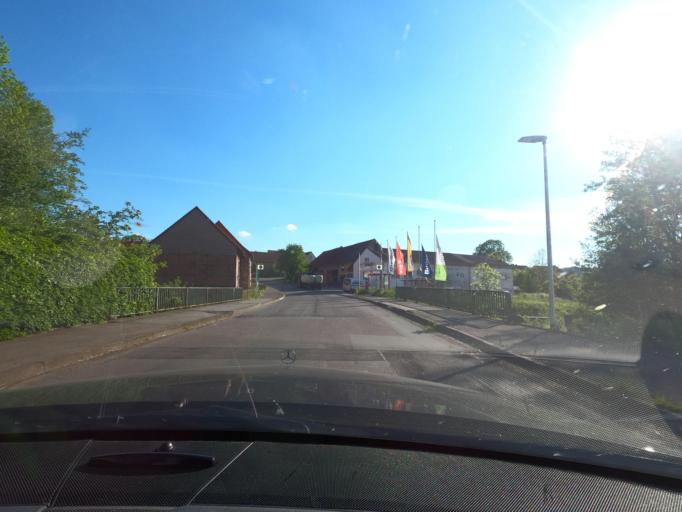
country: DE
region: Hesse
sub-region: Regierungsbezirk Kassel
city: Martinhagen
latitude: 51.3327
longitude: 9.2448
